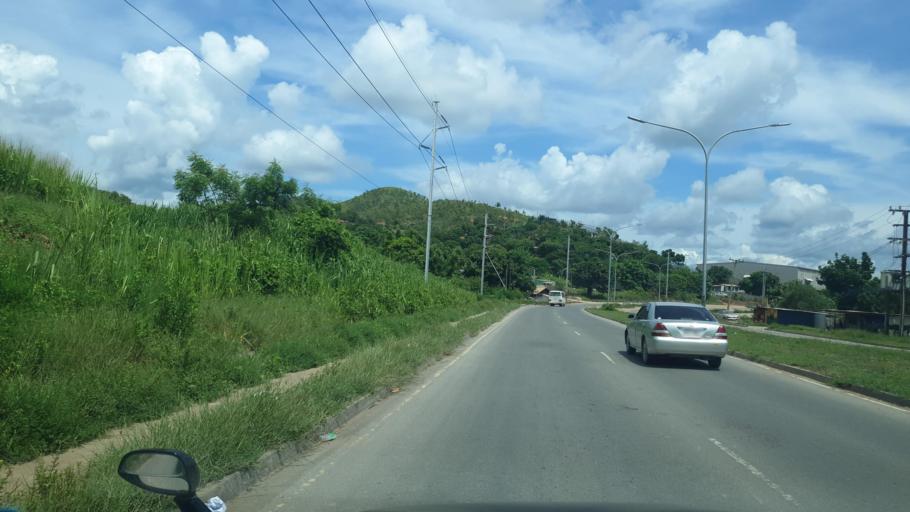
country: PG
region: National Capital
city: Port Moresby
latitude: -9.3909
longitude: 147.1534
